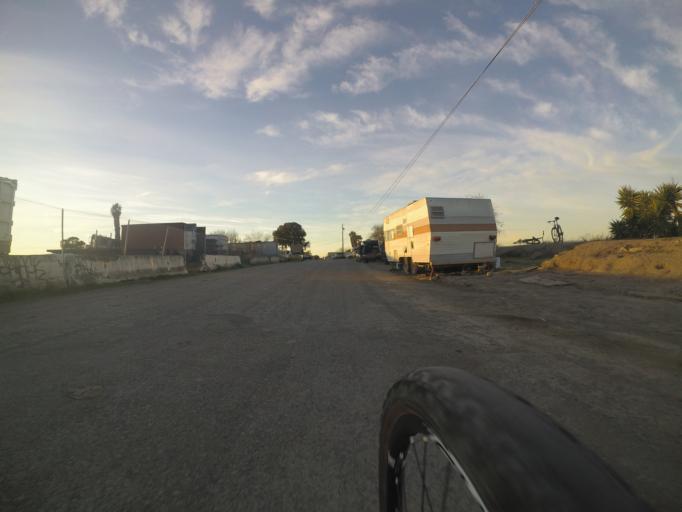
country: US
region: California
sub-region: Santa Clara County
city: Milpitas
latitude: 37.4347
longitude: -121.9689
